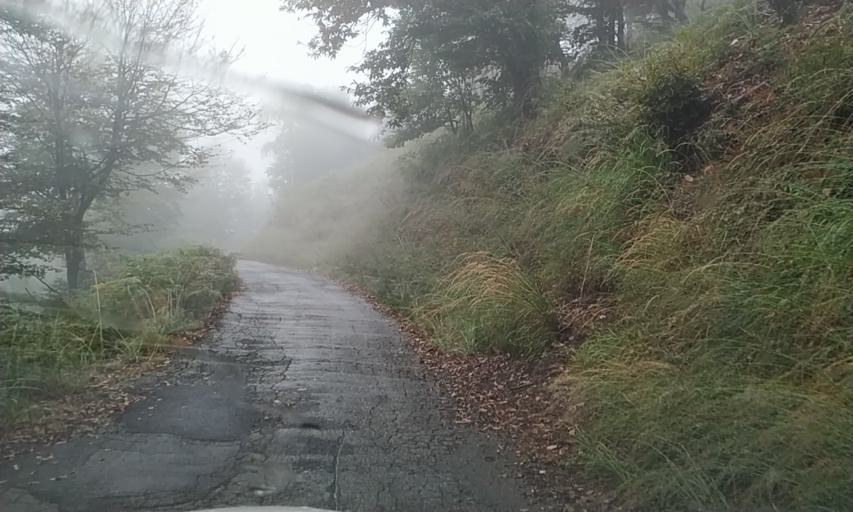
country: IT
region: Piedmont
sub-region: Provincia di Vercelli
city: Civiasco
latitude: 45.8299
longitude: 8.2998
